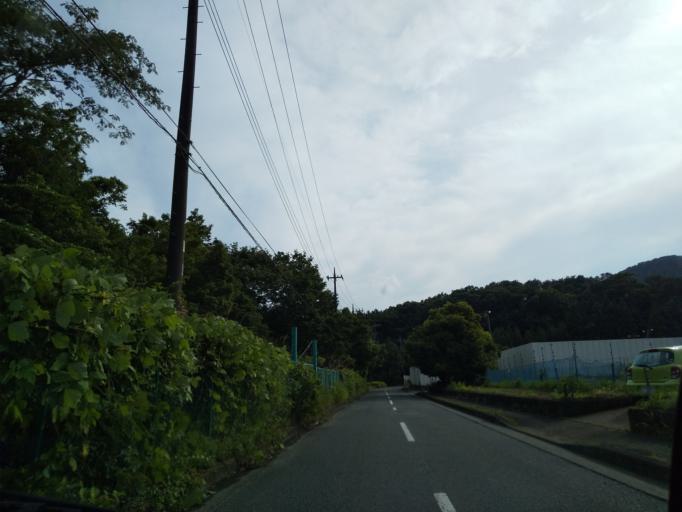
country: JP
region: Kanagawa
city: Atsugi
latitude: 35.4899
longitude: 139.3114
